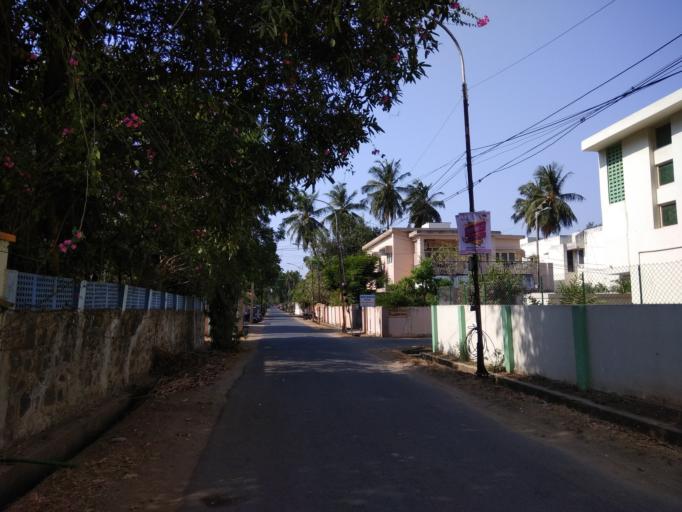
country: IN
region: Tamil Nadu
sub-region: Kancheepuram
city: Saint Thomas Mount
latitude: 13.0202
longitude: 80.1996
